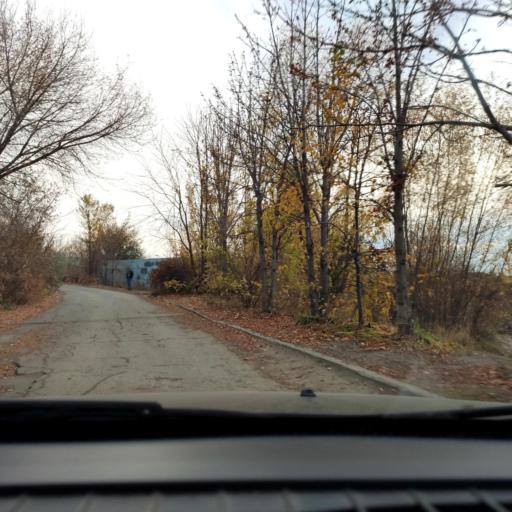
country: RU
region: Samara
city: Tol'yatti
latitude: 53.4983
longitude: 49.2624
